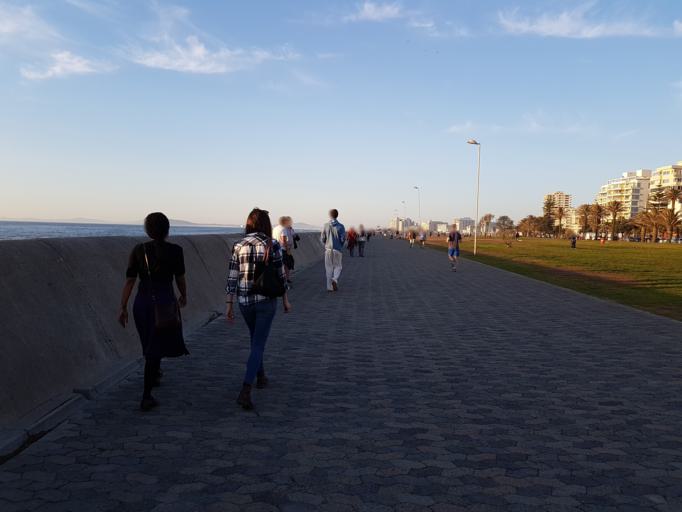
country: ZA
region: Western Cape
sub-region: City of Cape Town
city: Cape Town
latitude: -33.9110
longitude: 18.3887
